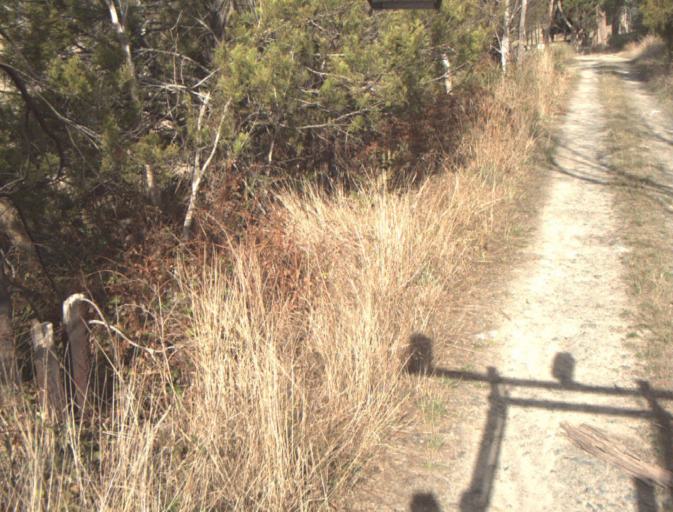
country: AU
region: Tasmania
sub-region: Launceston
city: Mayfield
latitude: -41.2210
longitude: 147.1576
